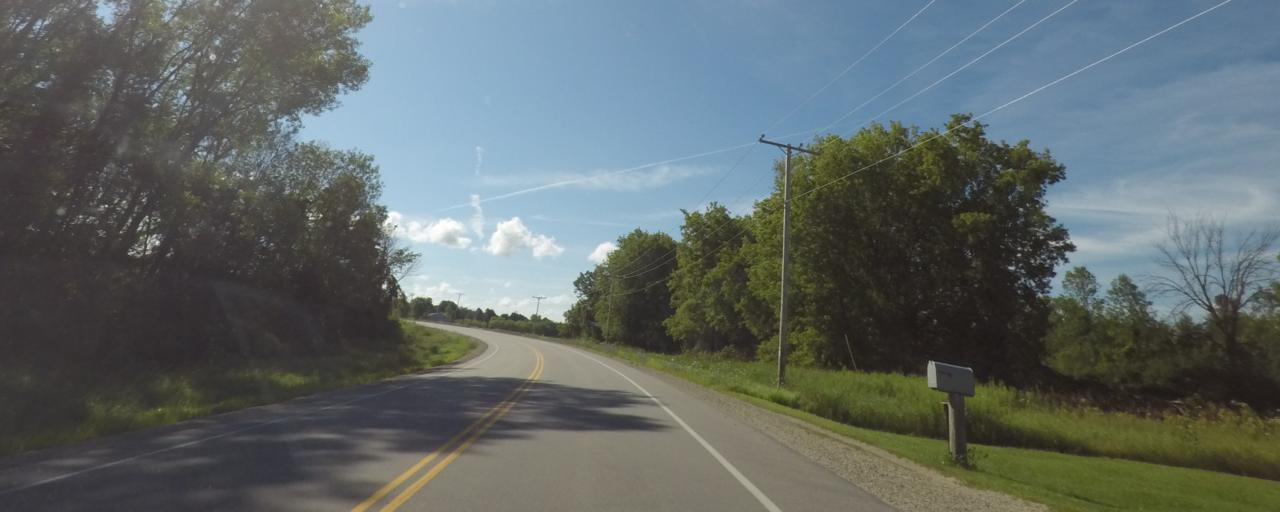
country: US
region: Wisconsin
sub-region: Jefferson County
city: Ixonia
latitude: 43.0706
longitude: -88.6352
